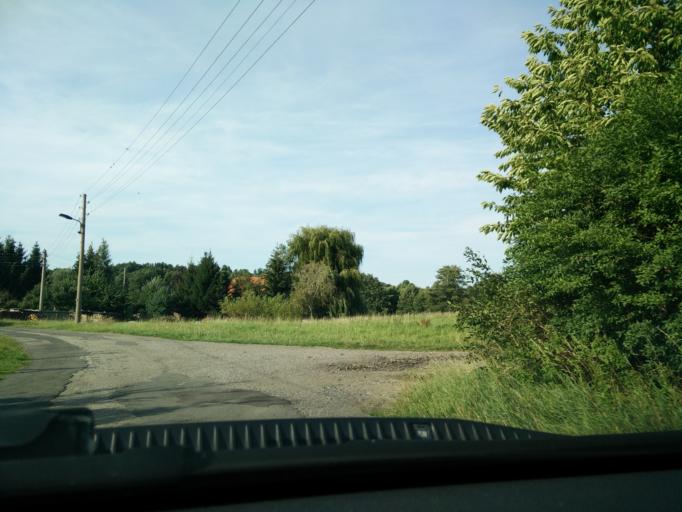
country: DE
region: Saxony
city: Bad Lausick
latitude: 51.1243
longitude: 12.6688
